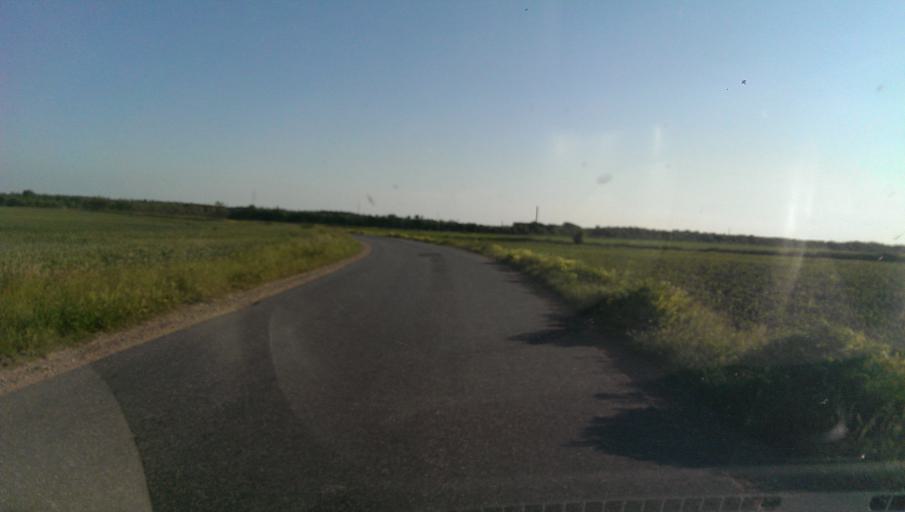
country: DK
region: South Denmark
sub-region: Esbjerg Kommune
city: Tjaereborg
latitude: 55.5075
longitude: 8.5748
